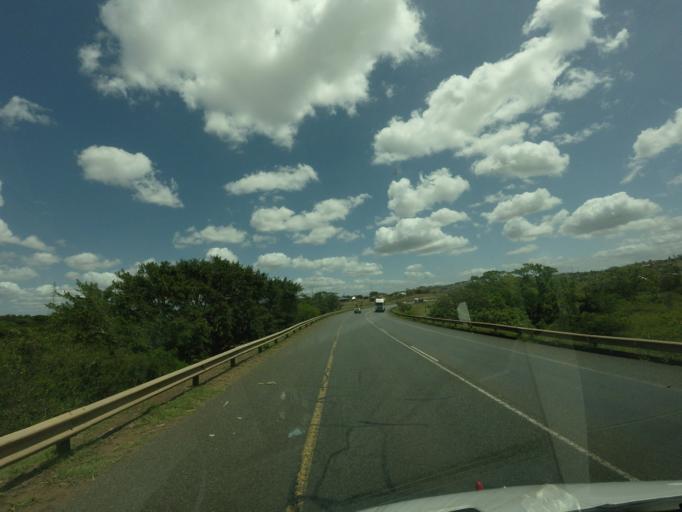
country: ZA
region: KwaZulu-Natal
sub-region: uMkhanyakude District Municipality
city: Mtubatuba
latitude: -28.4545
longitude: 32.1450
